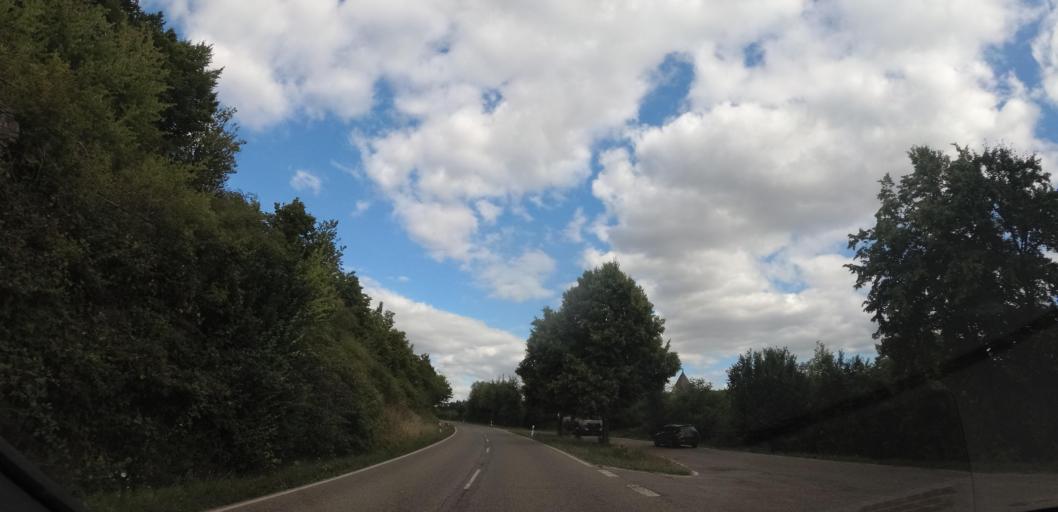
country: DE
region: Baden-Wuerttemberg
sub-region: Regierungsbezirk Stuttgart
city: Neudenau
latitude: 49.2906
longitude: 9.2835
